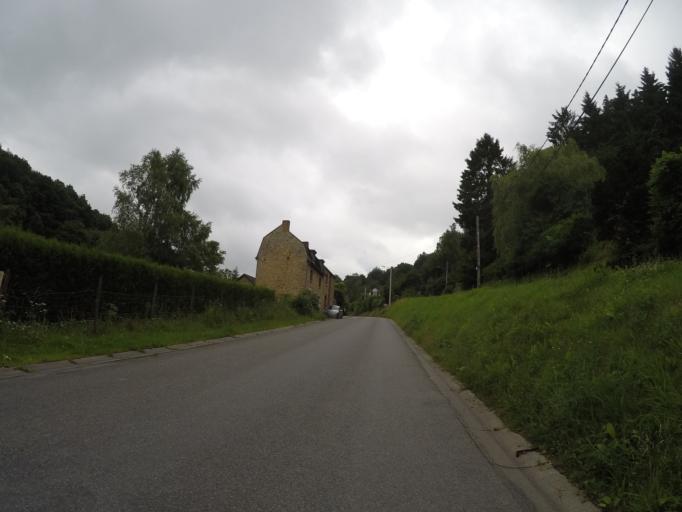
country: BE
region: Wallonia
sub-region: Province de Namur
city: Assesse
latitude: 50.3455
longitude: 4.9568
